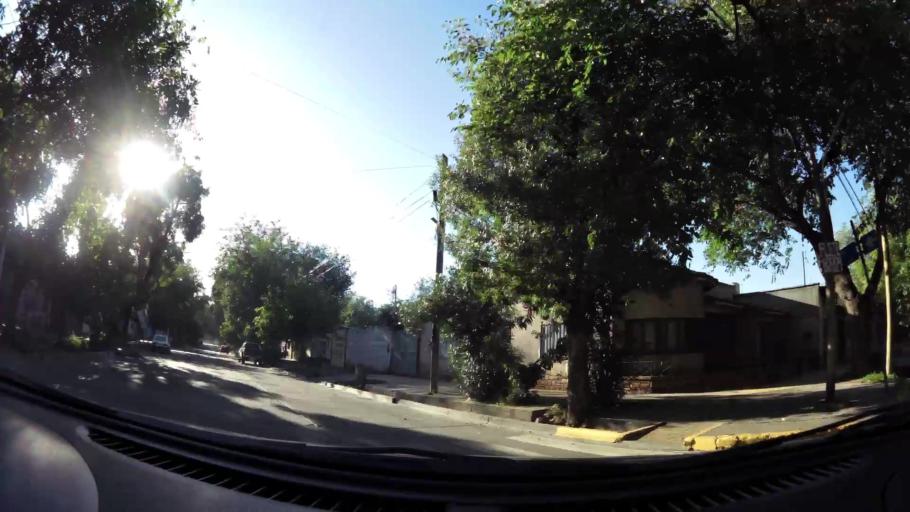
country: AR
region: Mendoza
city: Mendoza
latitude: -32.8735
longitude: -68.8234
